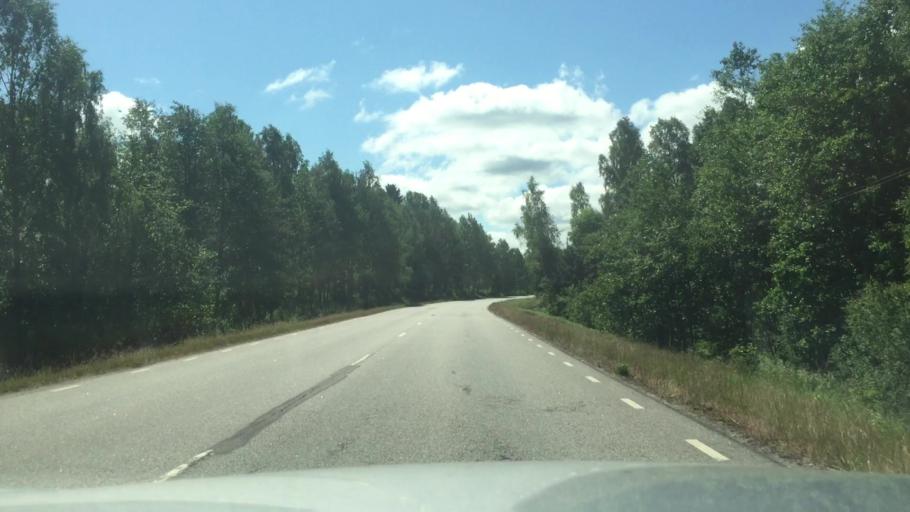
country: SE
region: Vaestra Goetaland
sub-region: Karlsborgs Kommun
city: Molltorp
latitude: 58.6270
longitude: 14.3887
